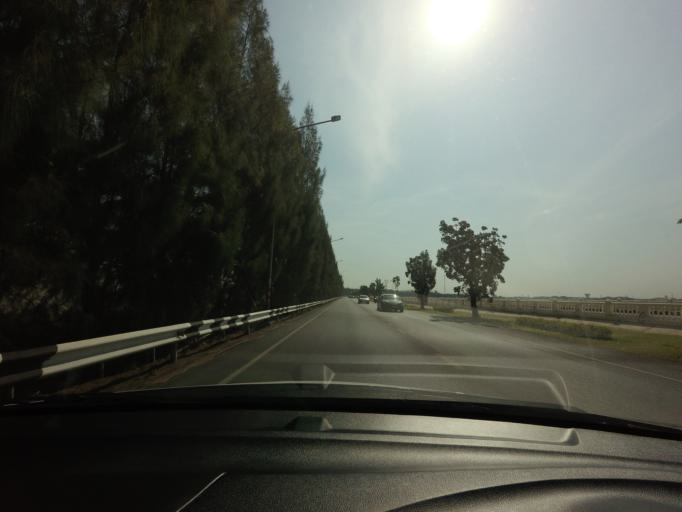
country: TH
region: Bangkok
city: Sai Mai
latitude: 13.9354
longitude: 100.6160
